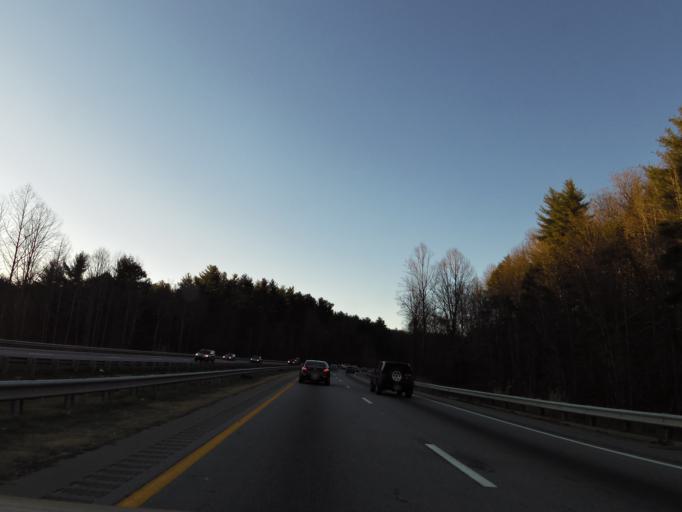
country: US
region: North Carolina
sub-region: Buncombe County
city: Bent Creek
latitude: 35.5136
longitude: -82.5860
